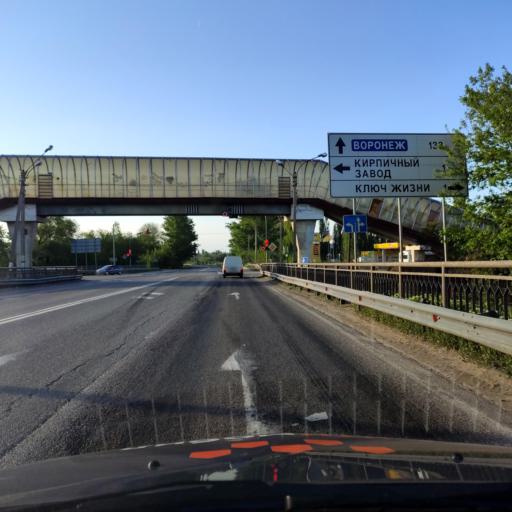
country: RU
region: Lipetsk
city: Yelets
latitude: 52.6004
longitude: 38.4727
